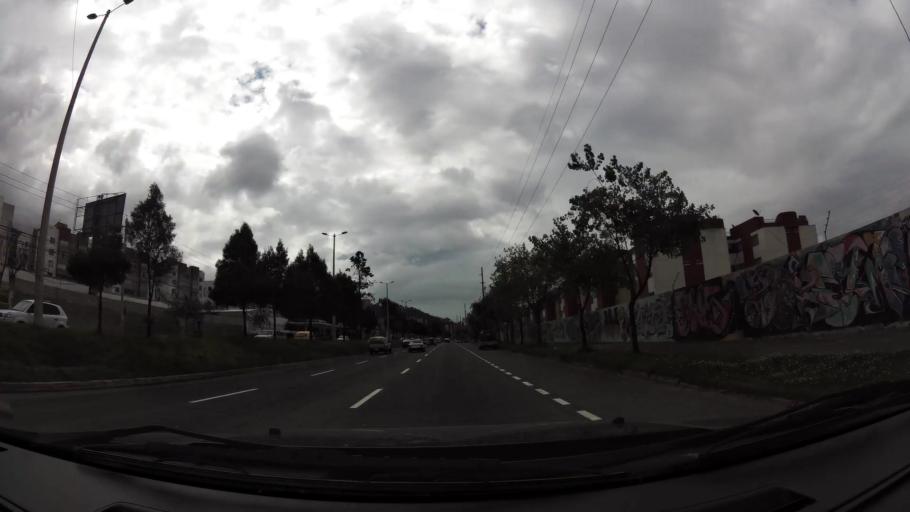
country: EC
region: Pichincha
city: Quito
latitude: -0.1471
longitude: -78.4987
